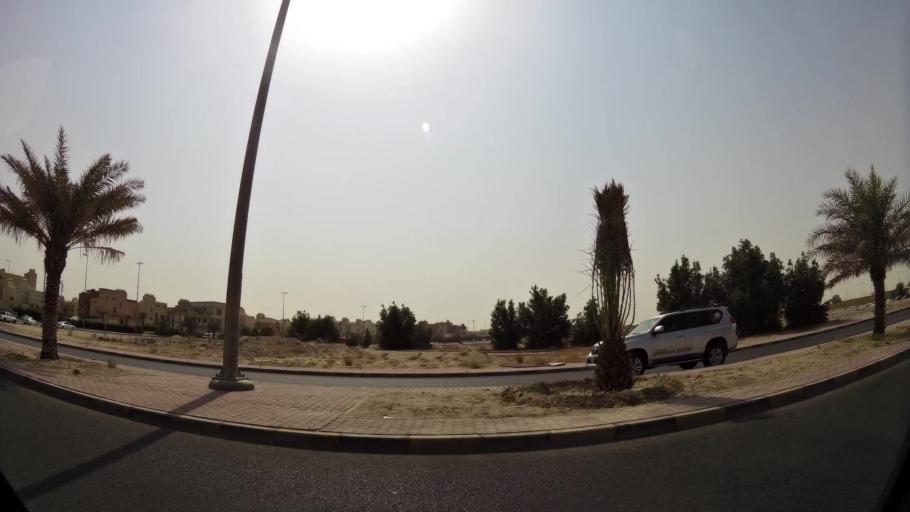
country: KW
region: Muhafazat al Jahra'
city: Al Jahra'
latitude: 29.3202
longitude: 47.7119
